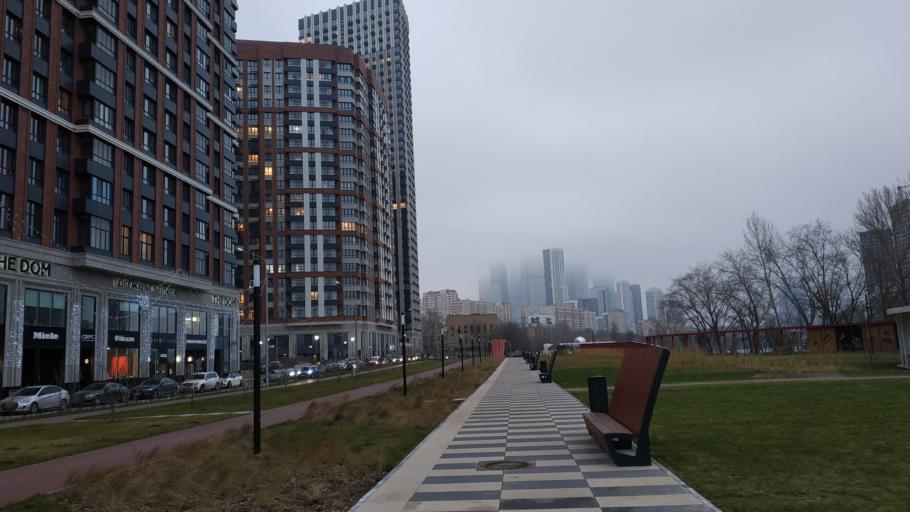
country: RU
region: Moskovskaya
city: Fili
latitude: 55.7621
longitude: 37.5100
